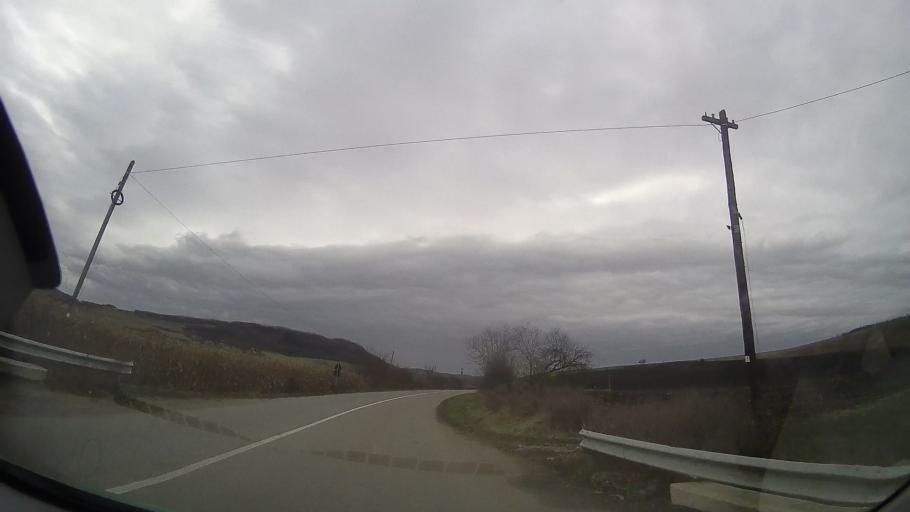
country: RO
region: Bistrita-Nasaud
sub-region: Comuna Milas
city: Milas
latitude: 46.8058
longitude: 24.4282
